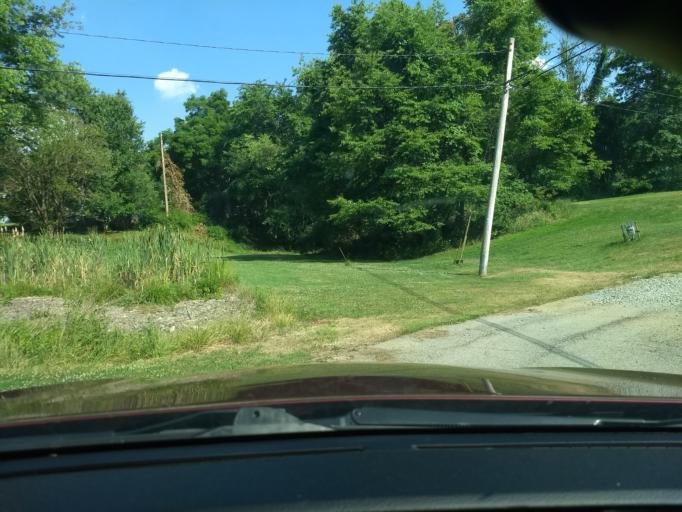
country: US
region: Pennsylvania
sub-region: Allegheny County
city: Clairton
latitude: 40.2677
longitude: -79.8439
